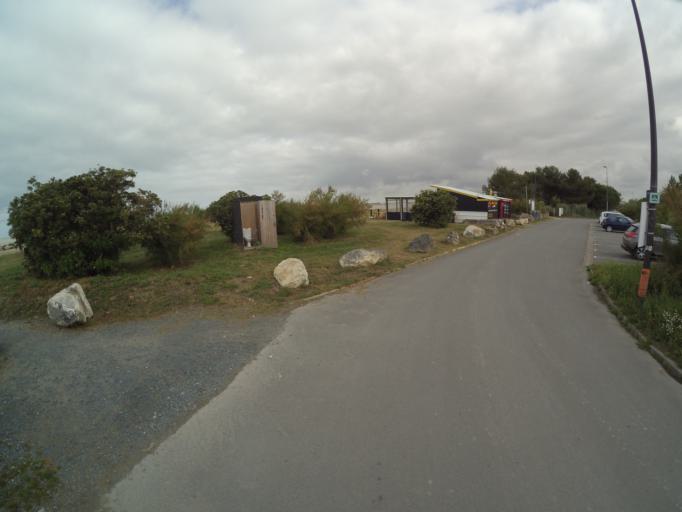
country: FR
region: Poitou-Charentes
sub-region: Departement de la Charente-Maritime
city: Angoulins
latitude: 46.1131
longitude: -1.1234
